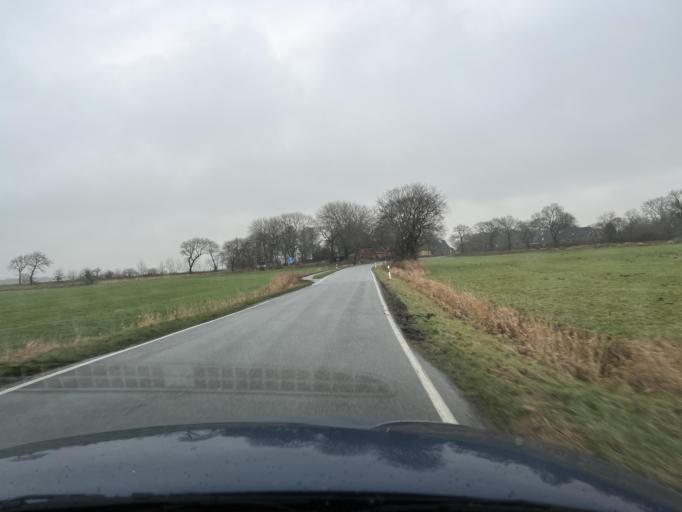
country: DE
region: Schleswig-Holstein
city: Lohe-Rickelshof
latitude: 54.2199
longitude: 9.0582
